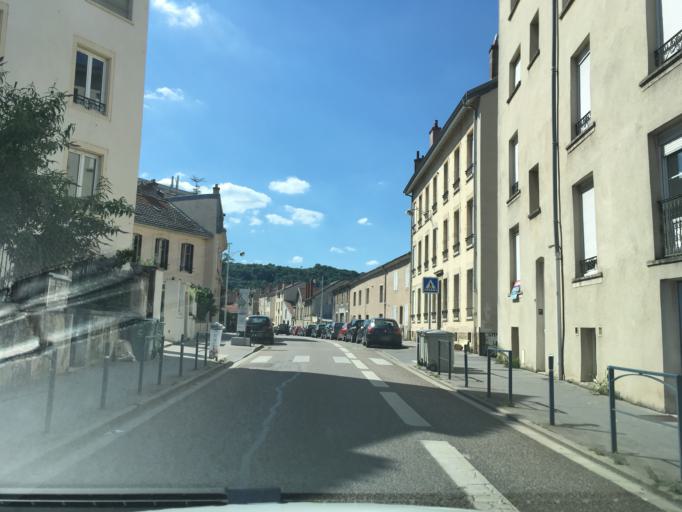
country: FR
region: Lorraine
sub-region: Departement de Meurthe-et-Moselle
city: Maxeville
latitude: 48.7035
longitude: 6.1735
